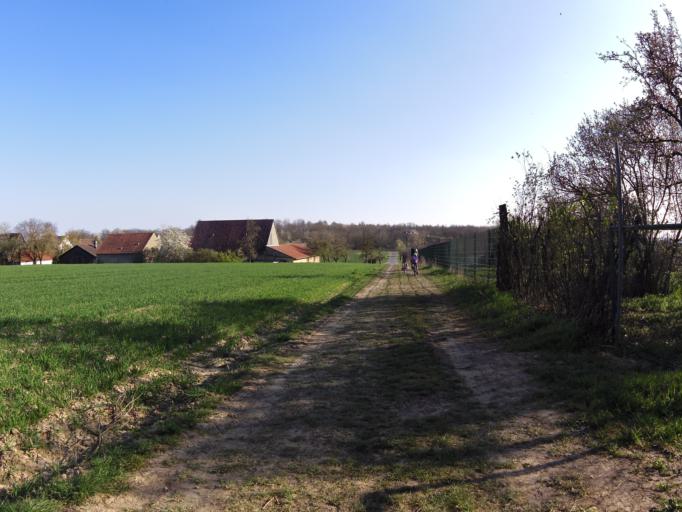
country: DE
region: Bavaria
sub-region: Regierungsbezirk Unterfranken
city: Kurnach
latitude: 49.8251
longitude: 10.0609
